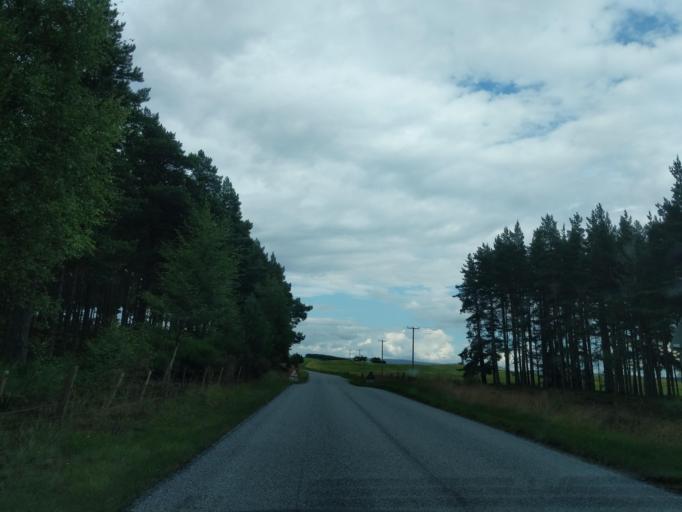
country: GB
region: Scotland
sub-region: Highland
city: Grantown on Spey
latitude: 57.3067
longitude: -3.7188
